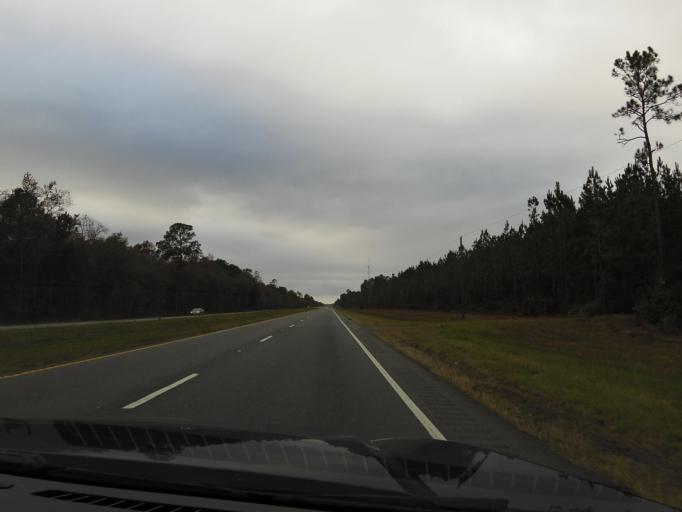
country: US
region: Georgia
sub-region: Charlton County
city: Folkston
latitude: 30.8985
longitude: -82.0591
